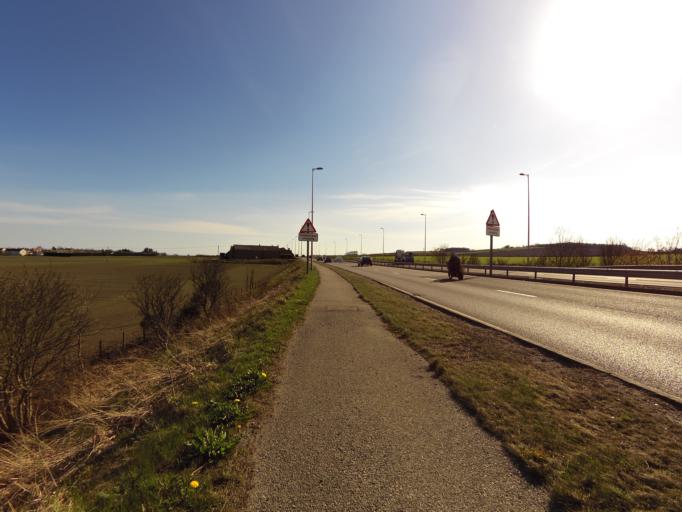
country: GB
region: Scotland
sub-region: Aberdeenshire
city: Newtonhill
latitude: 57.0268
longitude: -2.1657
